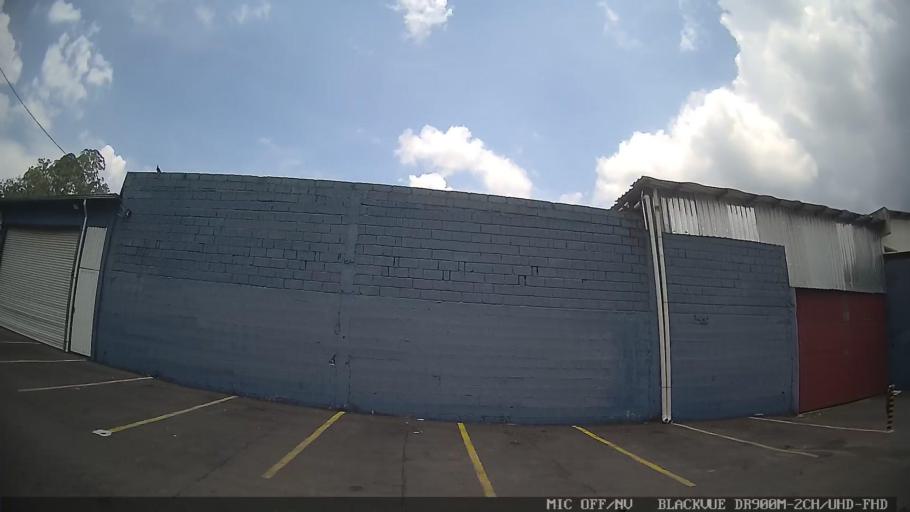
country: BR
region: Sao Paulo
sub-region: Ribeirao Pires
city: Ribeirao Pires
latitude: -23.6502
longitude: -46.3667
